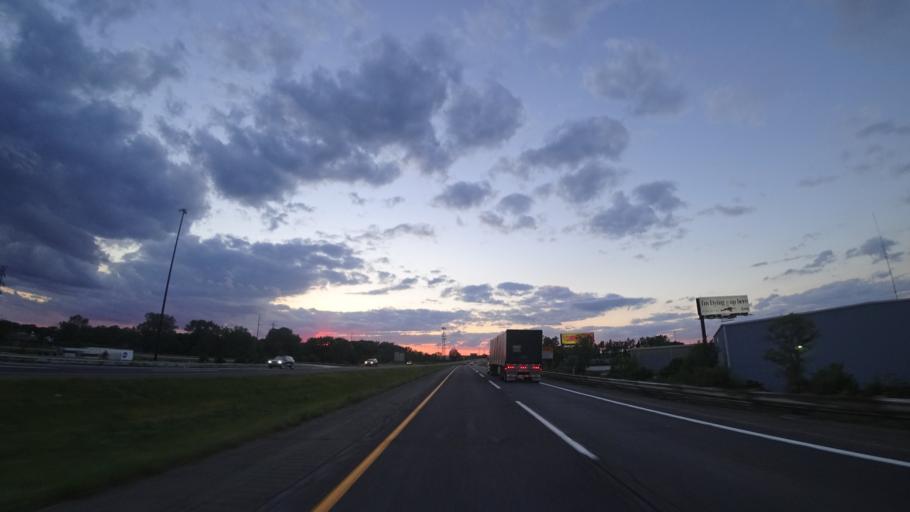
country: US
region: Illinois
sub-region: Cook County
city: Calumet City
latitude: 41.6459
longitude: -87.5094
